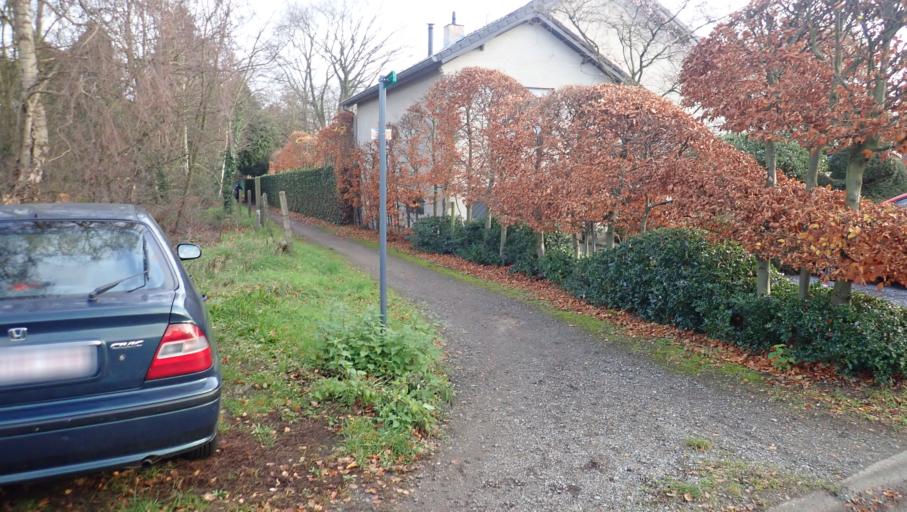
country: BE
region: Flanders
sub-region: Provincie Antwerpen
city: Schilde
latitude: 51.2131
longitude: 4.5952
